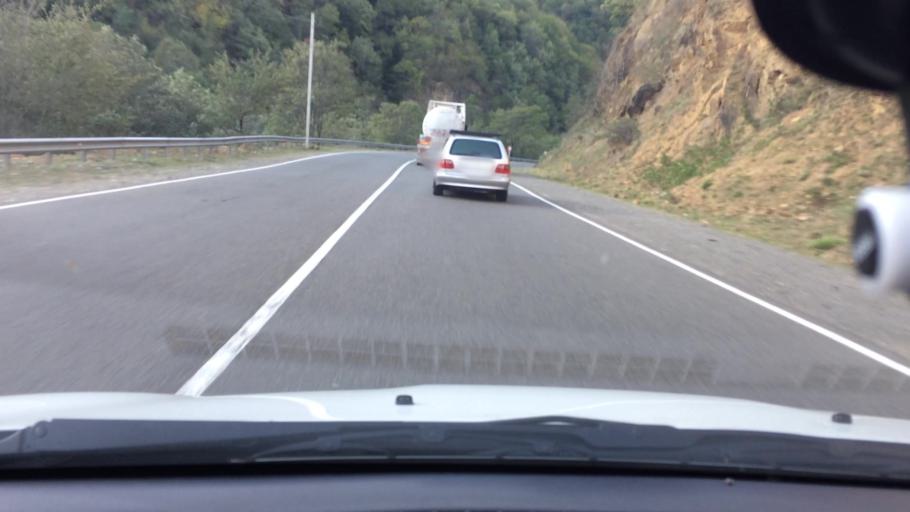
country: GE
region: Imereti
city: Kharagauli
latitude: 42.1063
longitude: 43.2474
